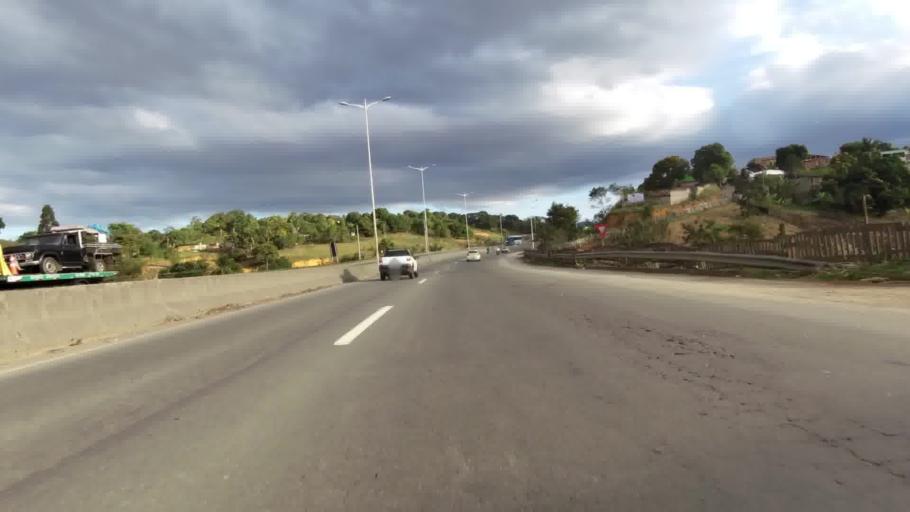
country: BR
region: Espirito Santo
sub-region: Vitoria
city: Vitoria
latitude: -20.2590
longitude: -40.3777
